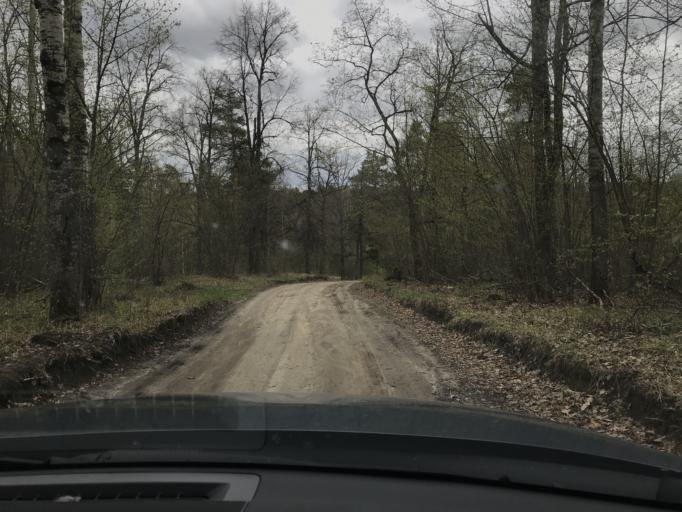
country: RU
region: Mordoviya
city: Shiringushi
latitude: 53.8555
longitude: 42.7859
